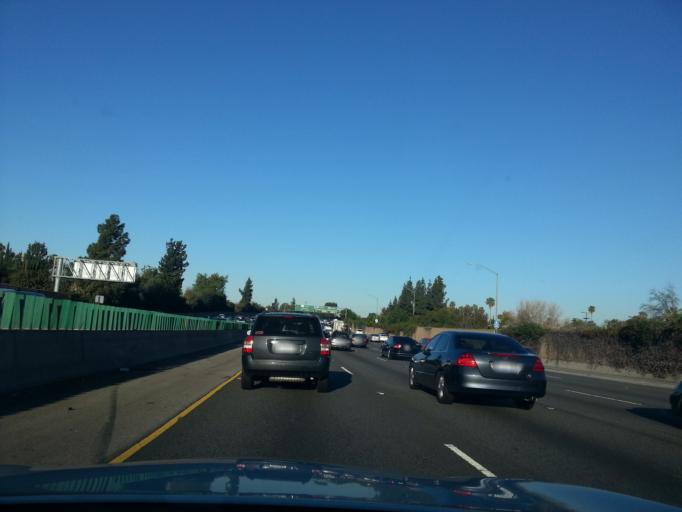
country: US
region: California
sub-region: Los Angeles County
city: Sherman Oaks
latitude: 34.1577
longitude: -118.4516
